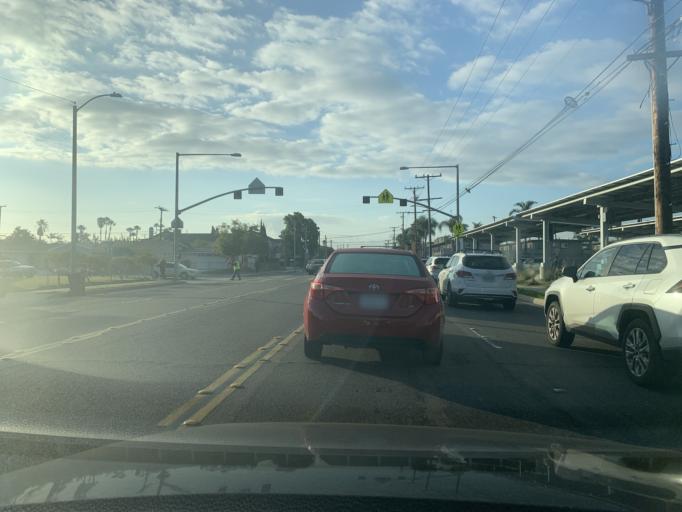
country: US
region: California
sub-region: Orange County
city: Westminster
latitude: 33.7635
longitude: -118.0160
